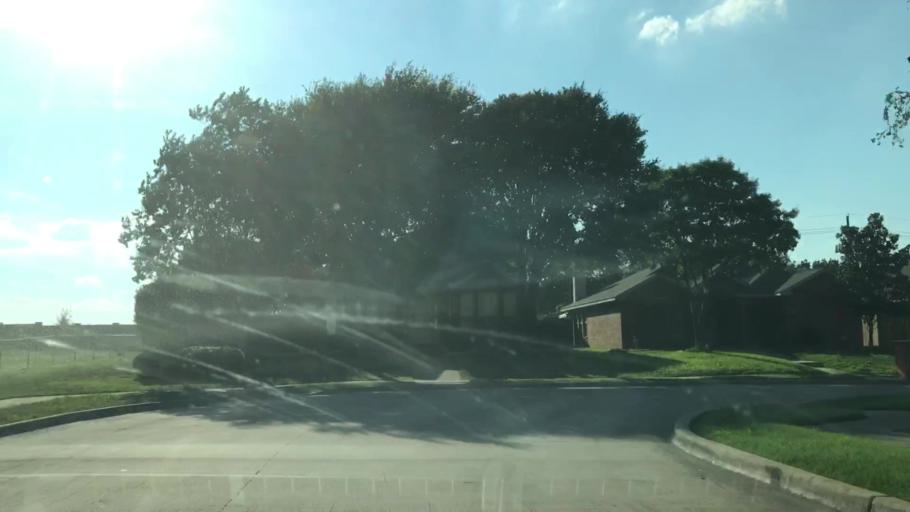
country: US
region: Texas
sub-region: Denton County
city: Lewisville
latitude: 33.0076
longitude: -97.0110
